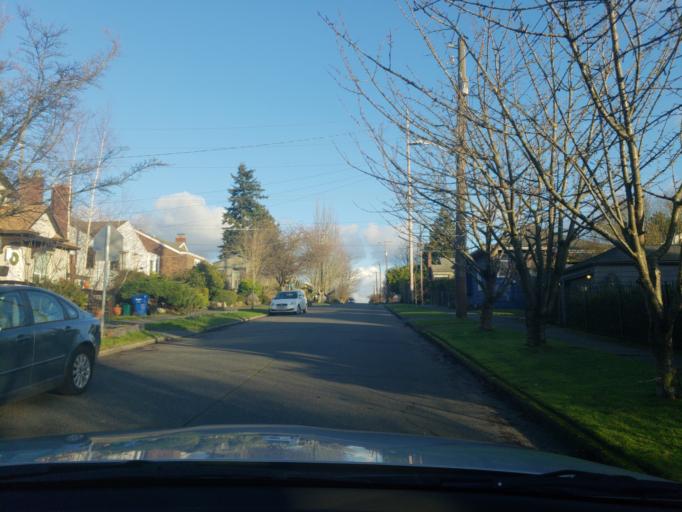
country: US
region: Washington
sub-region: King County
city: Shoreline
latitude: 47.6833
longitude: -122.3713
